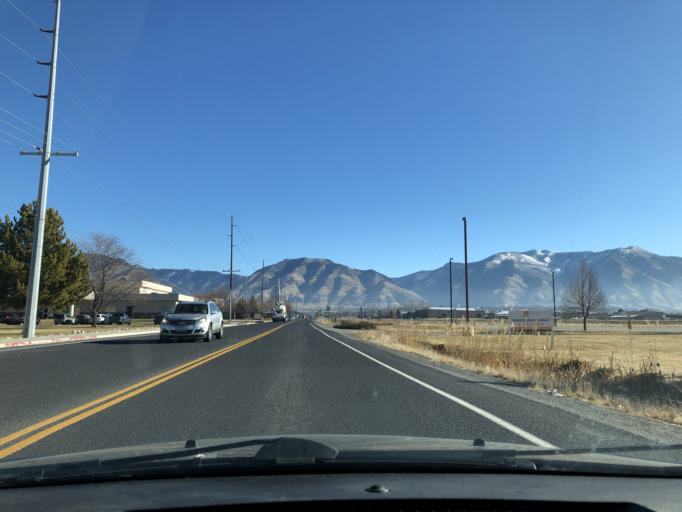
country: US
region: Utah
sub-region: Cache County
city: Logan
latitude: 41.7579
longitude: -111.8573
